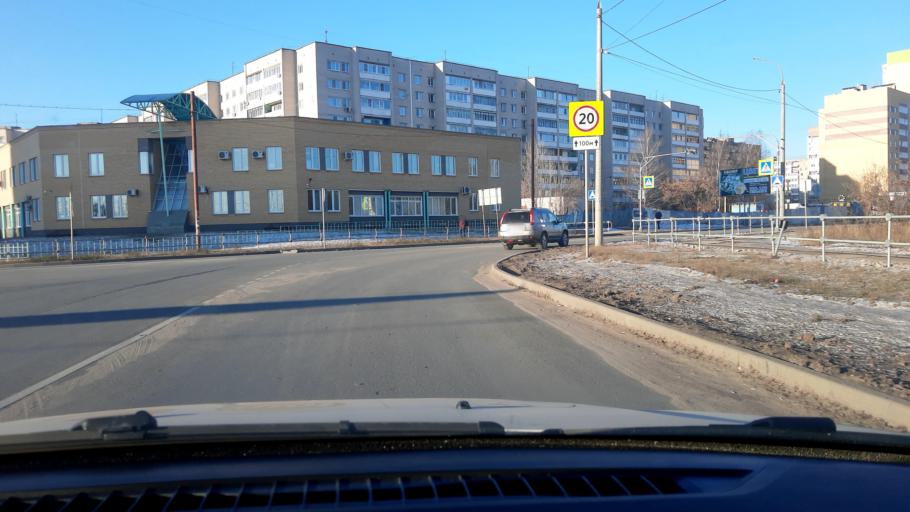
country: RU
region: Nizjnij Novgorod
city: Dzerzhinsk
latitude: 56.2283
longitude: 43.4128
